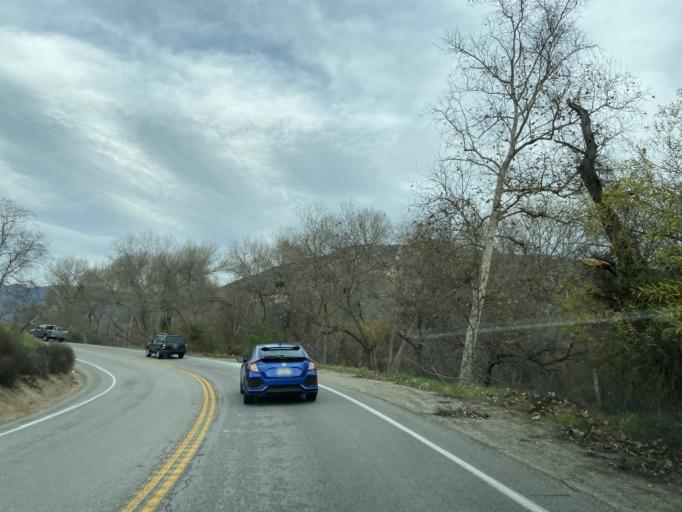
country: US
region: California
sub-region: San Diego County
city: Rainbow
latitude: 33.3439
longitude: -117.1196
